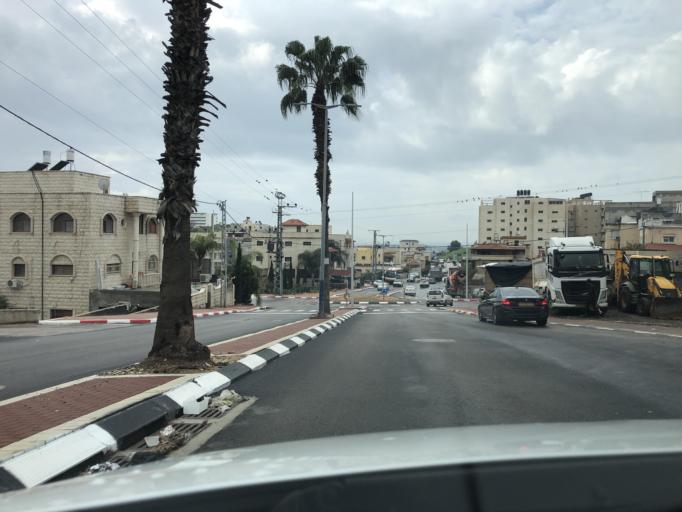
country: IL
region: Central District
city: Kafr Qasim
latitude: 32.1113
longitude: 34.9713
